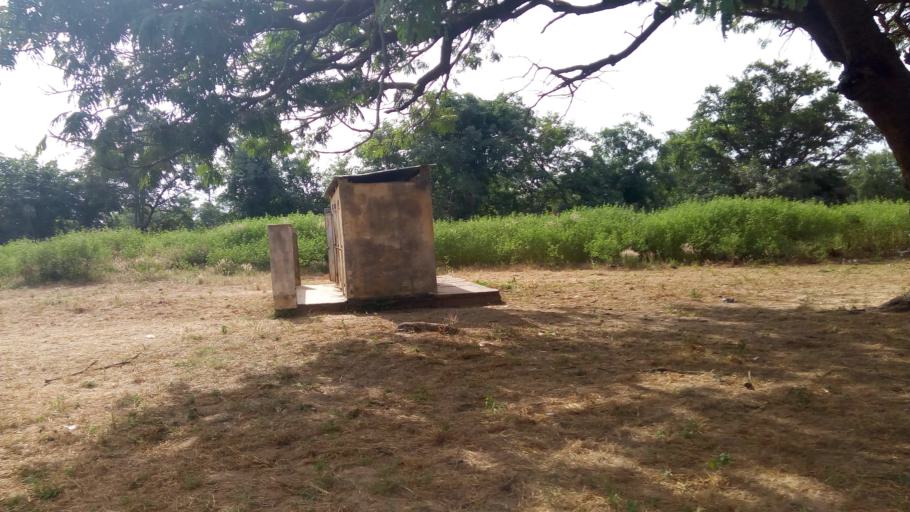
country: ML
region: Kayes
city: Kita
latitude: 13.1413
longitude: -8.8695
